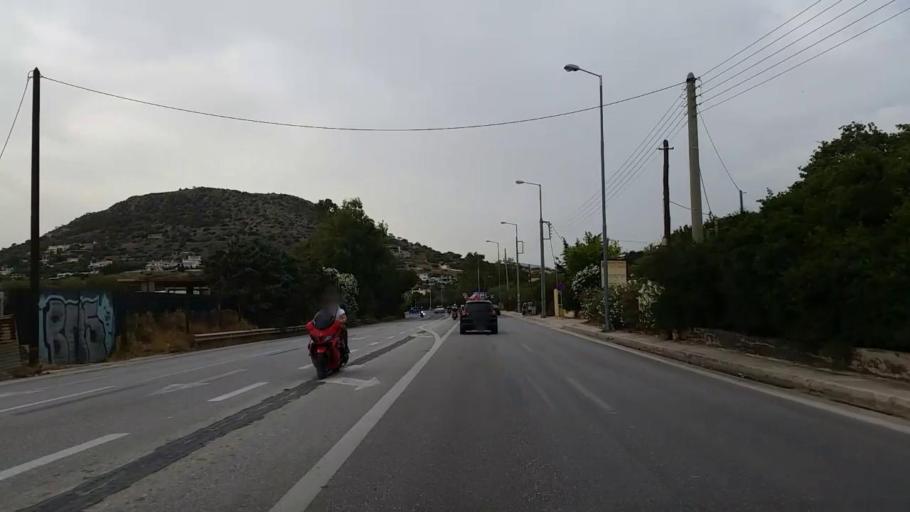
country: GR
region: Attica
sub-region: Nomarchia Anatolikis Attikis
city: Agios Dimitrios Kropias
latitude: 37.8002
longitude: 23.8701
